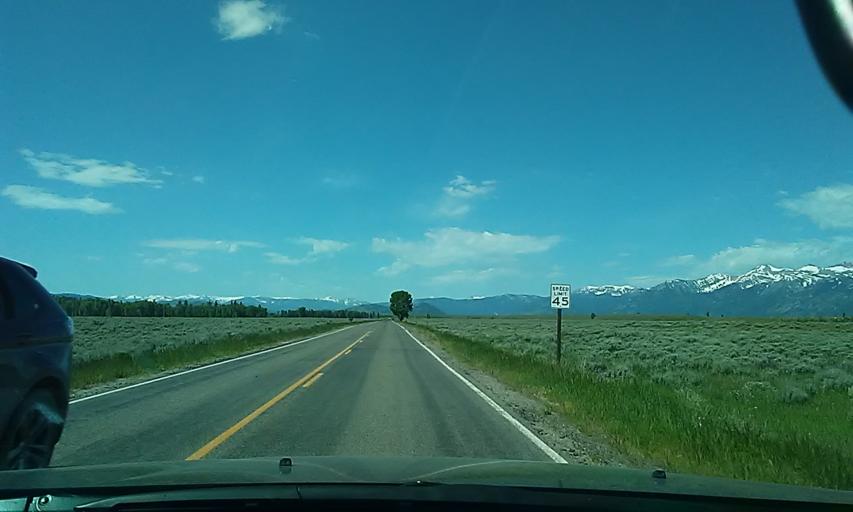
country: US
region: Wyoming
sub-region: Teton County
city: Jackson
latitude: 43.6193
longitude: -110.6720
